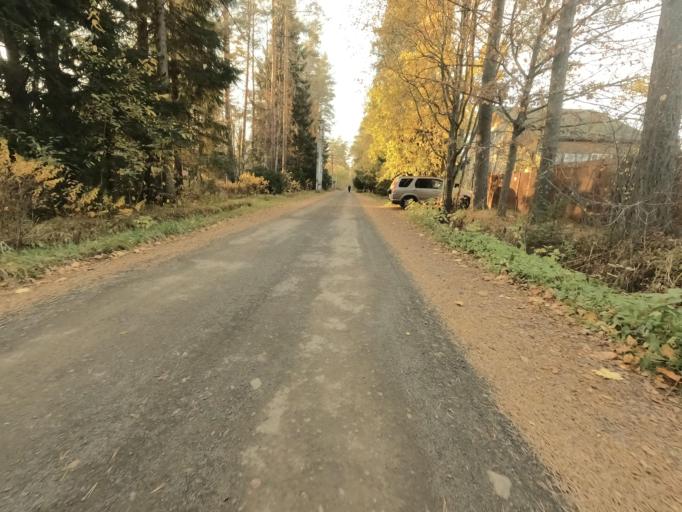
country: RU
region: St.-Petersburg
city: Beloostrov
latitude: 60.1707
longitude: 29.9849
